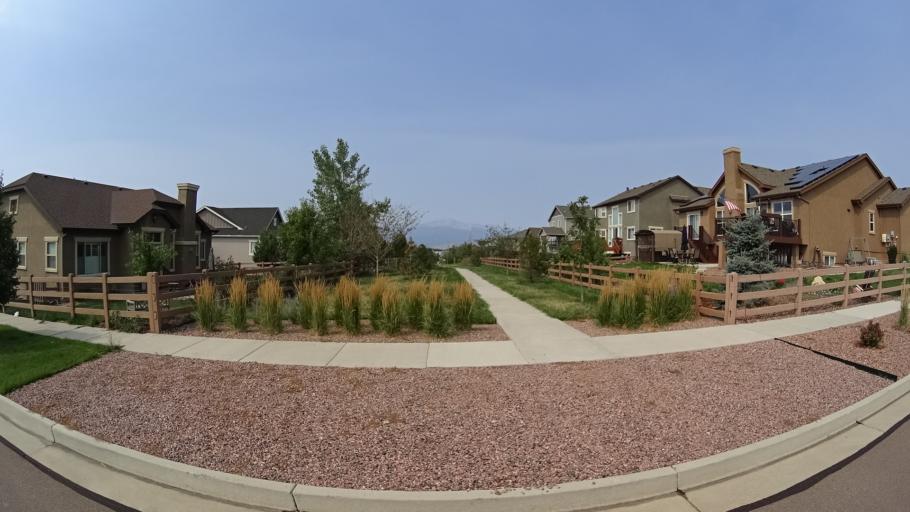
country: US
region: Colorado
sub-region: El Paso County
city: Black Forest
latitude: 38.9702
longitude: -104.7200
